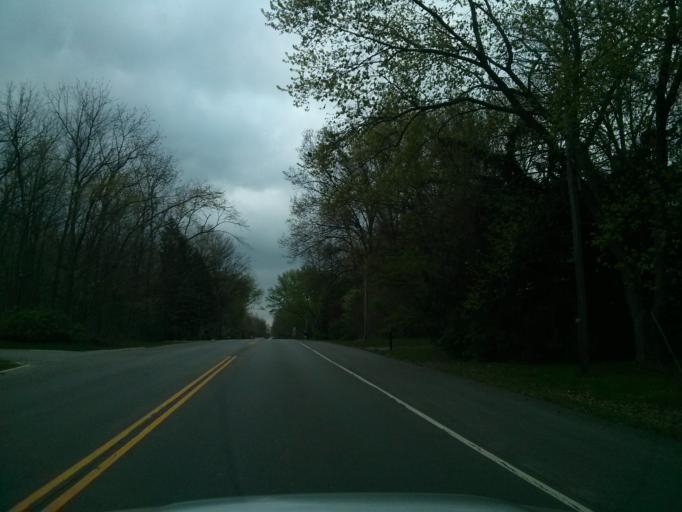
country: US
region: Indiana
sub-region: Hamilton County
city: Carmel
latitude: 39.9544
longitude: -86.1268
